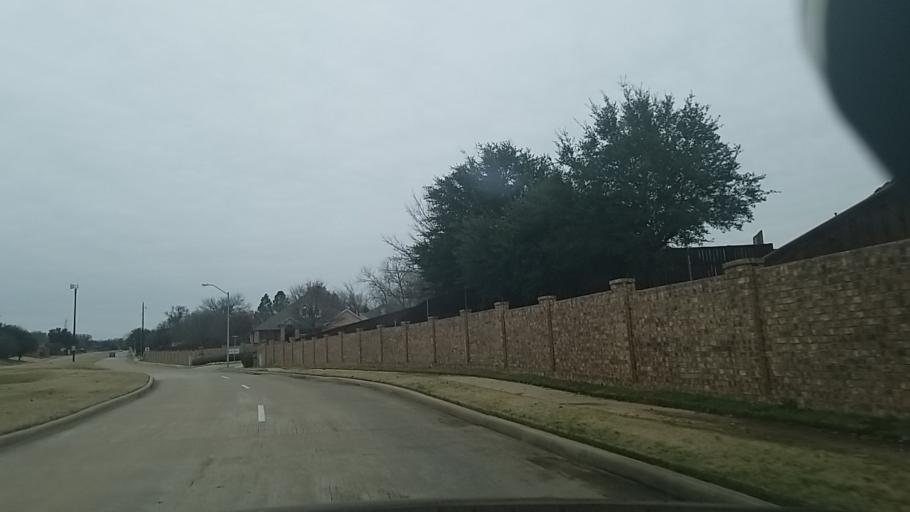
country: US
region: Texas
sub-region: Denton County
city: Corinth
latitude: 33.1343
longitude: -97.0735
